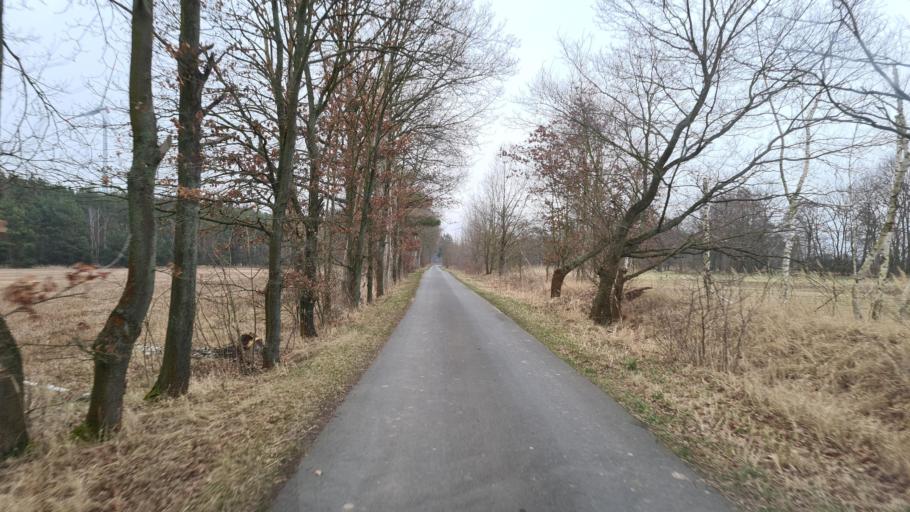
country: DE
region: Brandenburg
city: Herzberg
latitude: 51.6364
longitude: 13.2037
